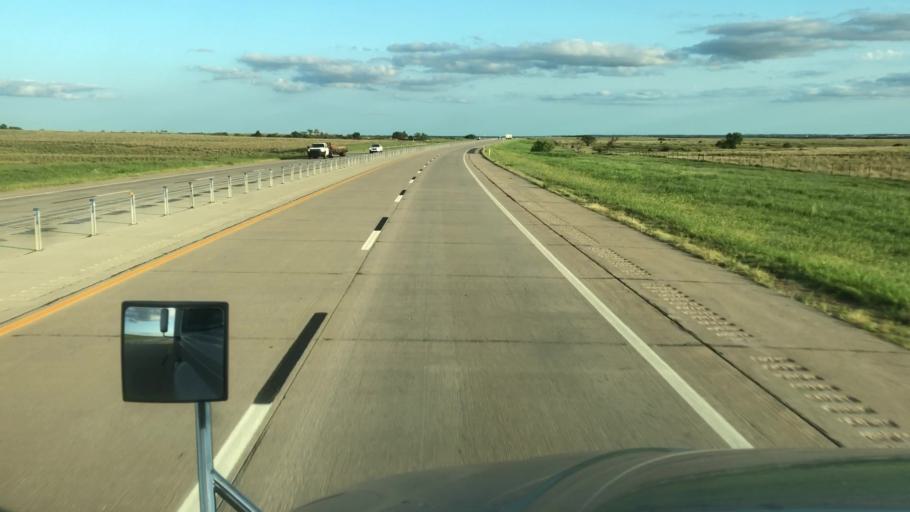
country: US
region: Oklahoma
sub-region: Pawnee County
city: Pawnee
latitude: 36.3675
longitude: -97.0356
